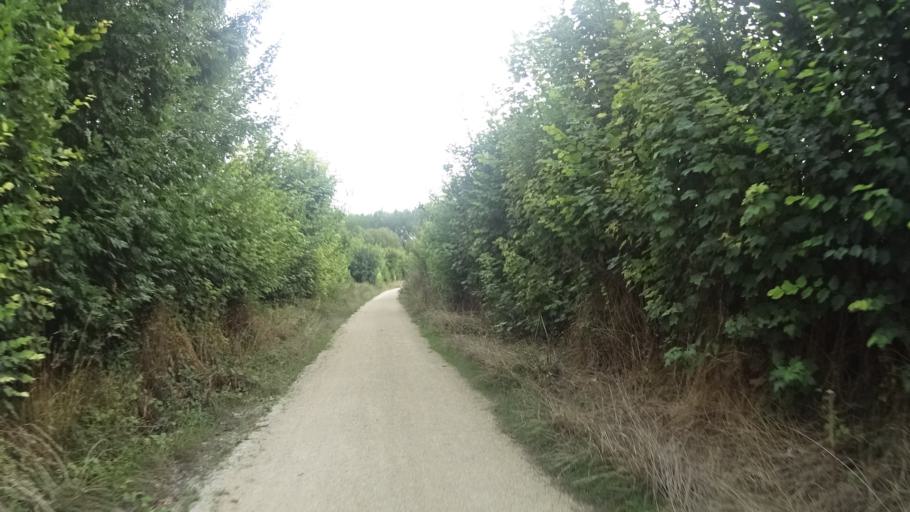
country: FR
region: Picardie
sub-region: Departement de l'Aisne
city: Origny-Sainte-Benoite
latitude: 49.8669
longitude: 3.5190
